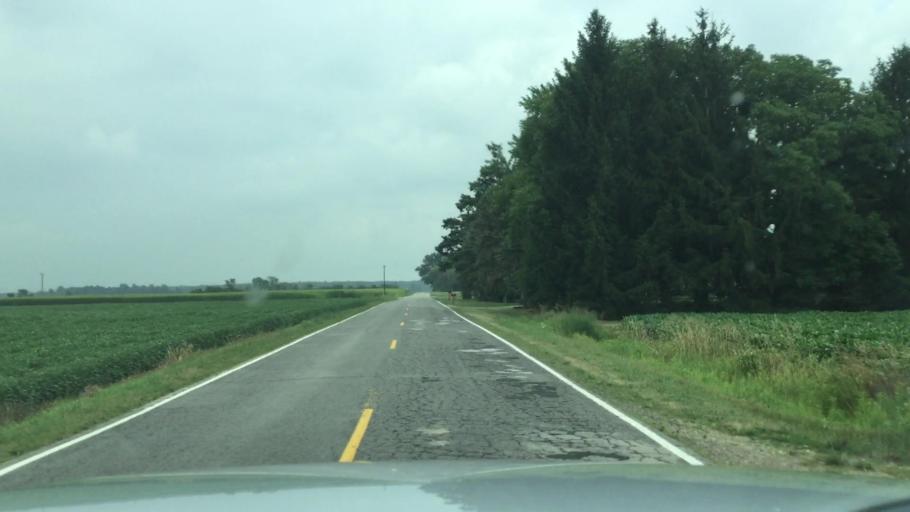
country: US
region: Michigan
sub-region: Shiawassee County
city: New Haven
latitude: 43.0735
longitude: -84.2261
